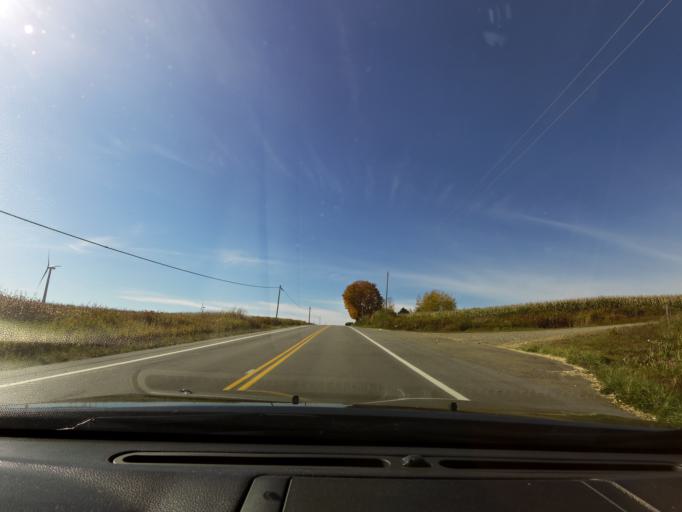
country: US
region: New York
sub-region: Wyoming County
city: Warsaw
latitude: 42.6383
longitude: -78.2316
